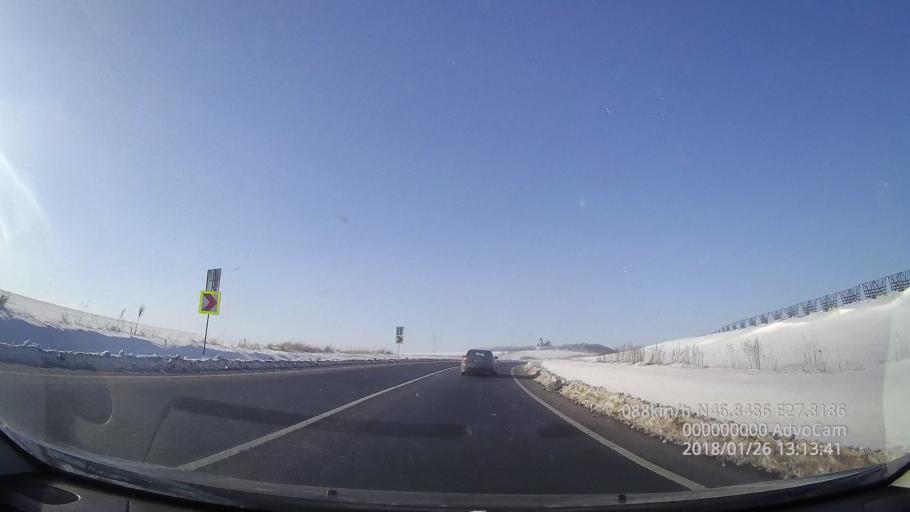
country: RO
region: Vaslui
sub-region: Comuna Miclesti
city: Chircesti
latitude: 46.8482
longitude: 27.8172
